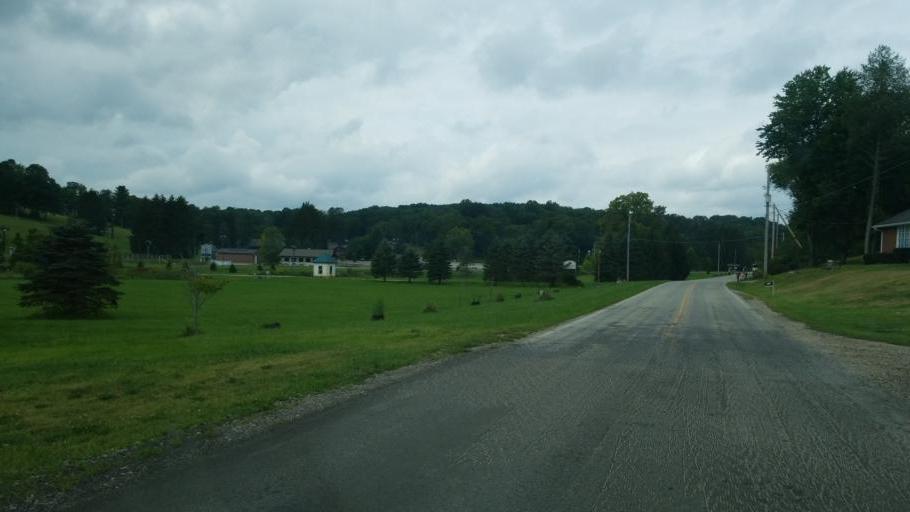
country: US
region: Ohio
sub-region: Sandusky County
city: Bellville
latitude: 40.6724
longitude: -82.4963
